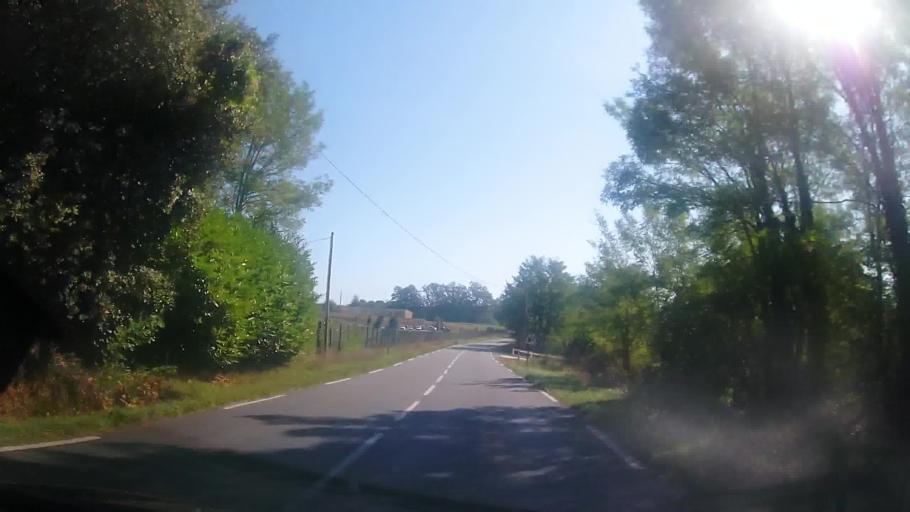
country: FR
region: Aquitaine
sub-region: Departement de la Dordogne
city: Carsac-Aillac
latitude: 44.8633
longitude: 1.2606
